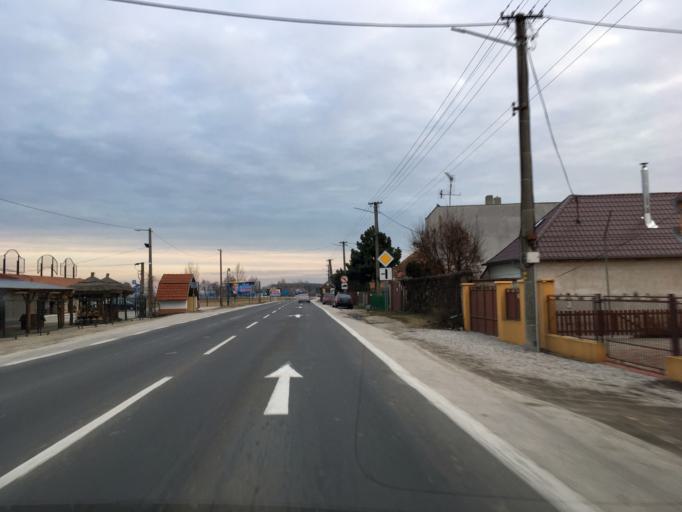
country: SK
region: Trnavsky
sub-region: Okres Dunajska Streda
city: Velky Meder
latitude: 47.9403
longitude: 17.7172
